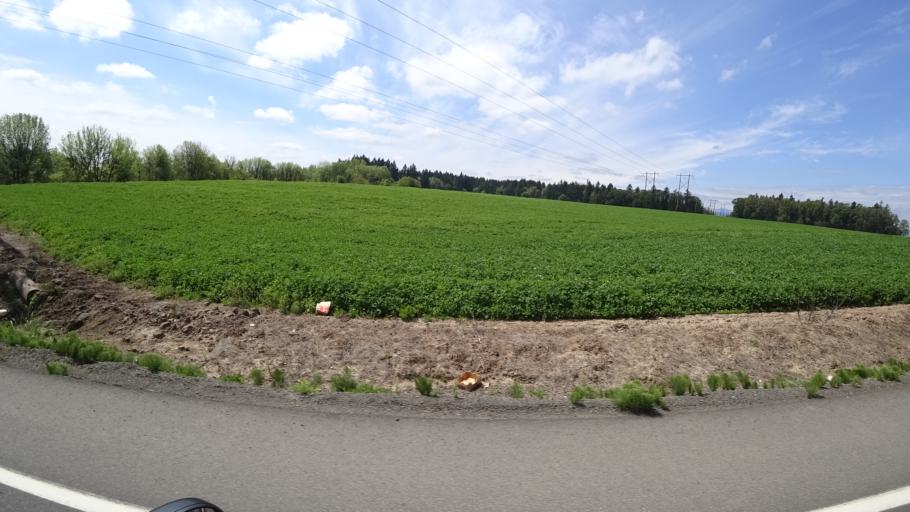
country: US
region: Oregon
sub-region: Washington County
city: Hillsboro
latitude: 45.5575
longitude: -122.9983
